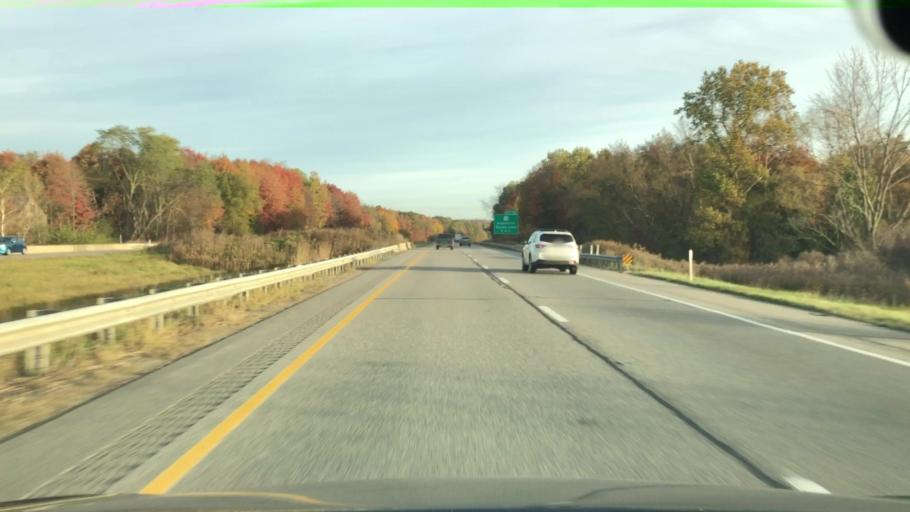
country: US
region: Pennsylvania
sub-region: Mercer County
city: Stoneboro
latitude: 41.3508
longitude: -80.1594
